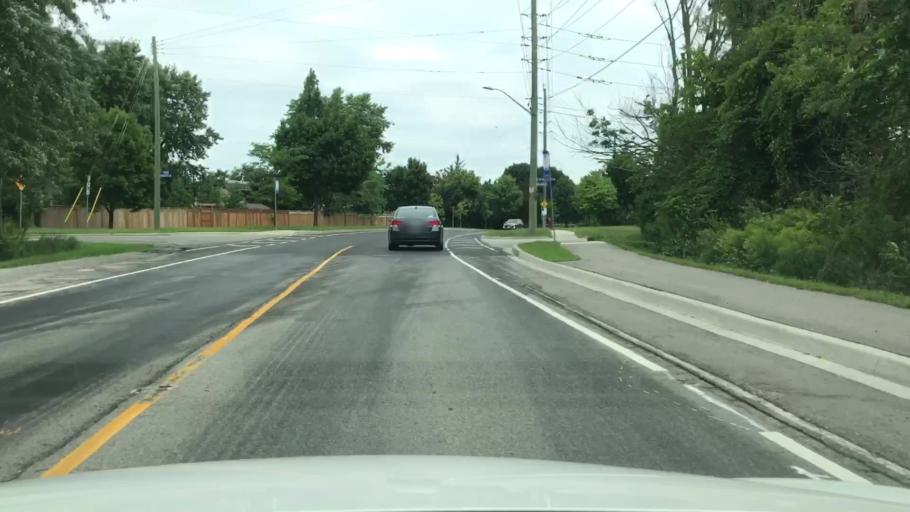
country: CA
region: Ontario
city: Newmarket
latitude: 44.0677
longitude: -79.4598
